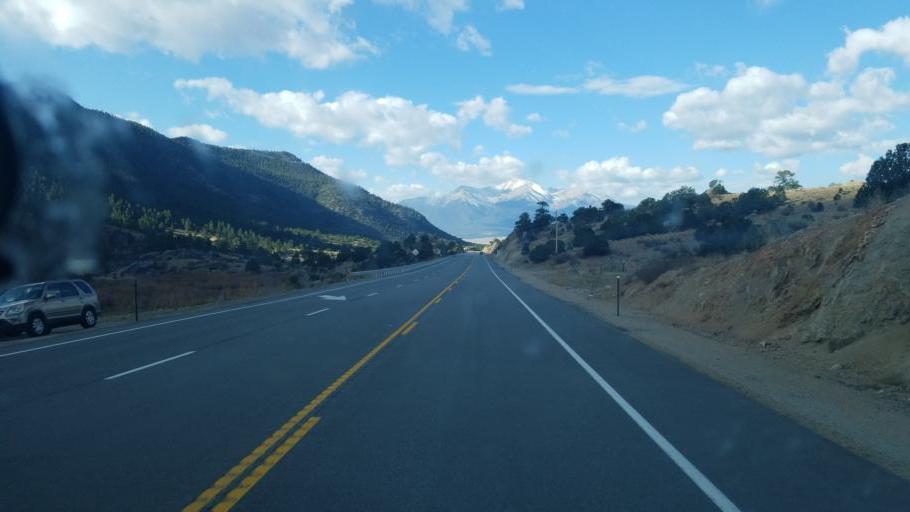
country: US
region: Colorado
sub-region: Chaffee County
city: Buena Vista
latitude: 38.8322
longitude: -106.0264
